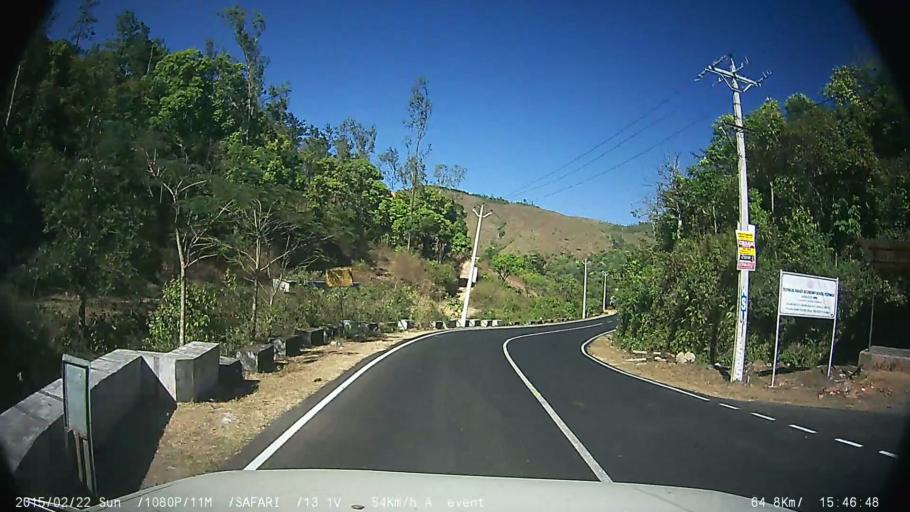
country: IN
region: Kerala
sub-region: Kottayam
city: Erattupetta
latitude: 9.5785
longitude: 76.9860
